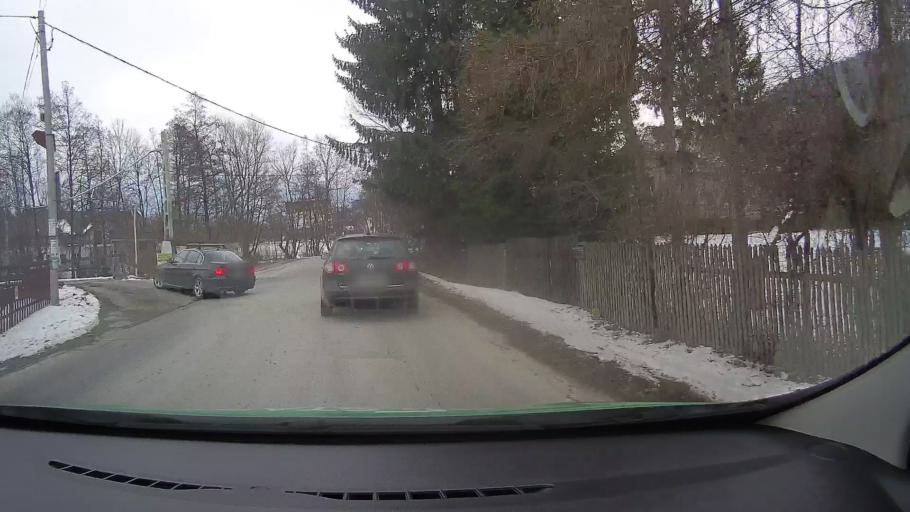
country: RO
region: Brasov
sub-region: Comuna Bran
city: Bran
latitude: 45.5226
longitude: 25.3661
